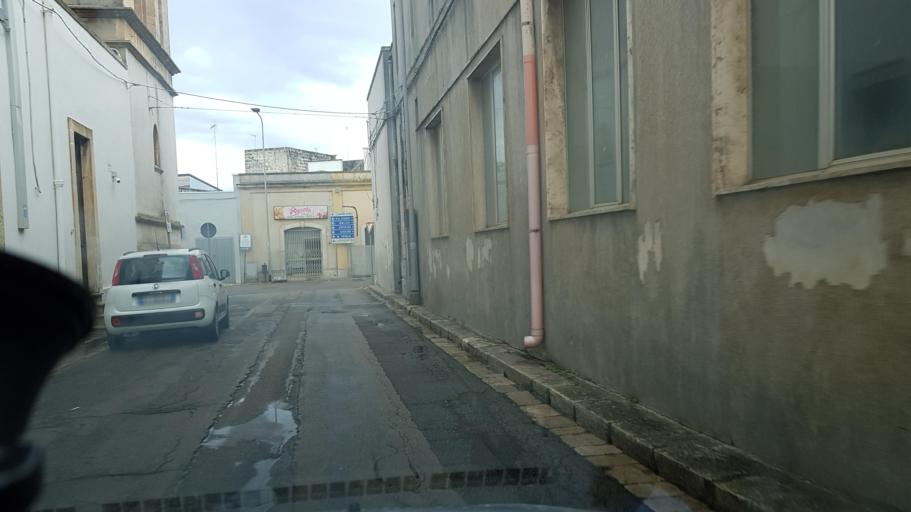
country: IT
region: Apulia
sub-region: Provincia di Lecce
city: Carmiano
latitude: 40.3447
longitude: 18.0461
